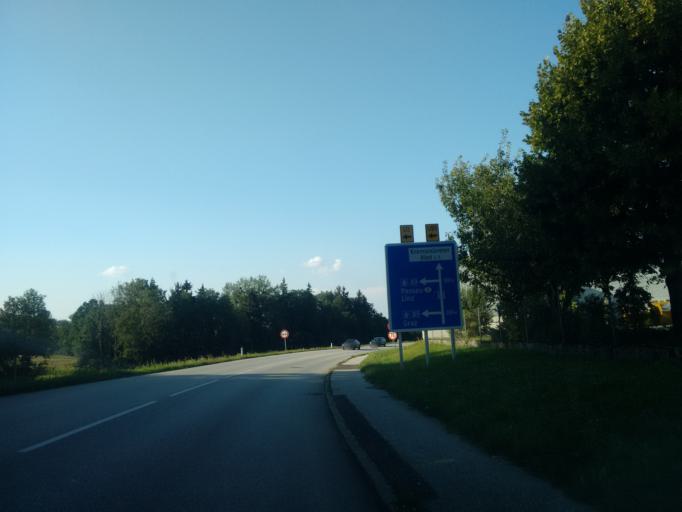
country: AT
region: Upper Austria
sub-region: Wels-Land
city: Sattledt
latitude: 48.0166
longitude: 14.0647
